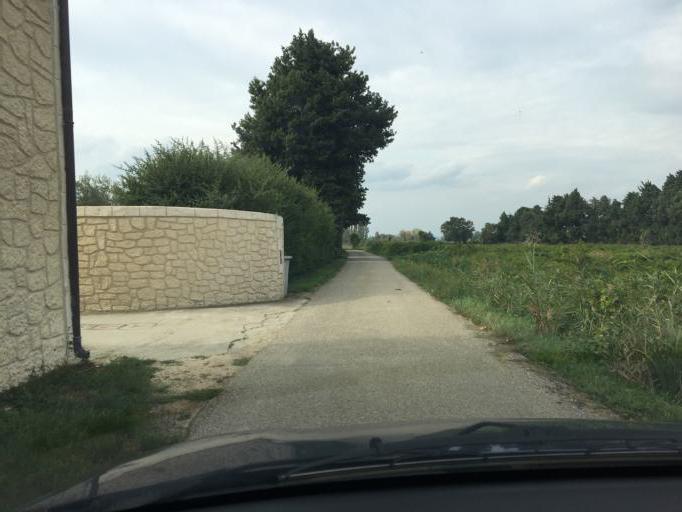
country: FR
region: Provence-Alpes-Cote d'Azur
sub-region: Departement du Vaucluse
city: Camaret-sur-Aigues
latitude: 44.1510
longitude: 4.8623
